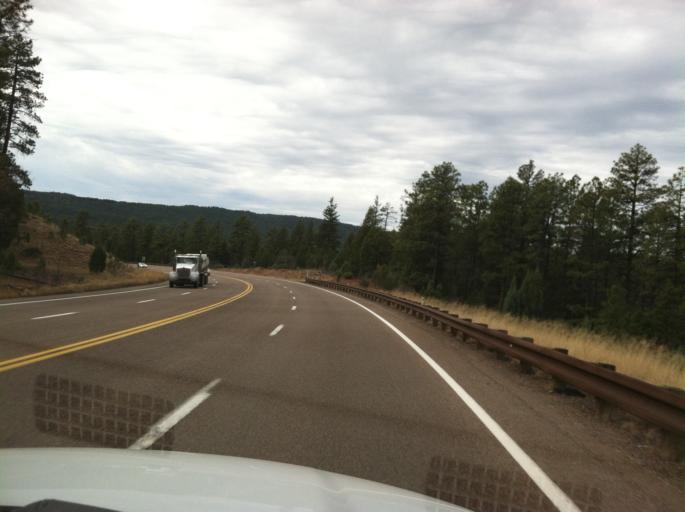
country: US
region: Arizona
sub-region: Gila County
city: Star Valley
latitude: 34.3007
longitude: -110.9603
